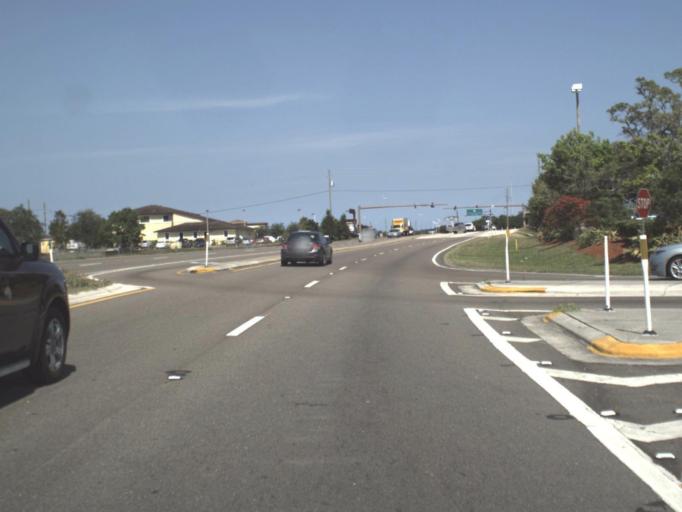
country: US
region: Florida
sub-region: Saint Johns County
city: Saint Augustine South
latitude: 29.8674
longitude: -81.3288
